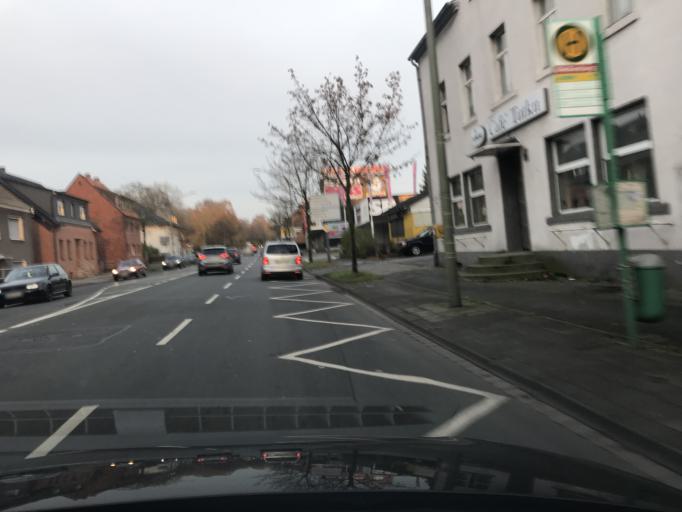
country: DE
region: North Rhine-Westphalia
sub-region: Regierungsbezirk Arnsberg
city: Hamm
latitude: 51.6969
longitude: 7.8276
